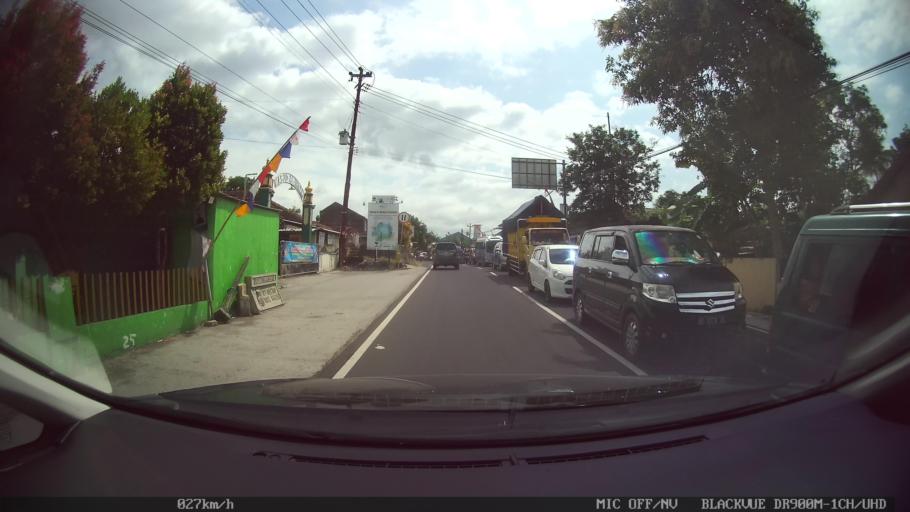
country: ID
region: Daerah Istimewa Yogyakarta
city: Depok
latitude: -7.8372
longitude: 110.4765
